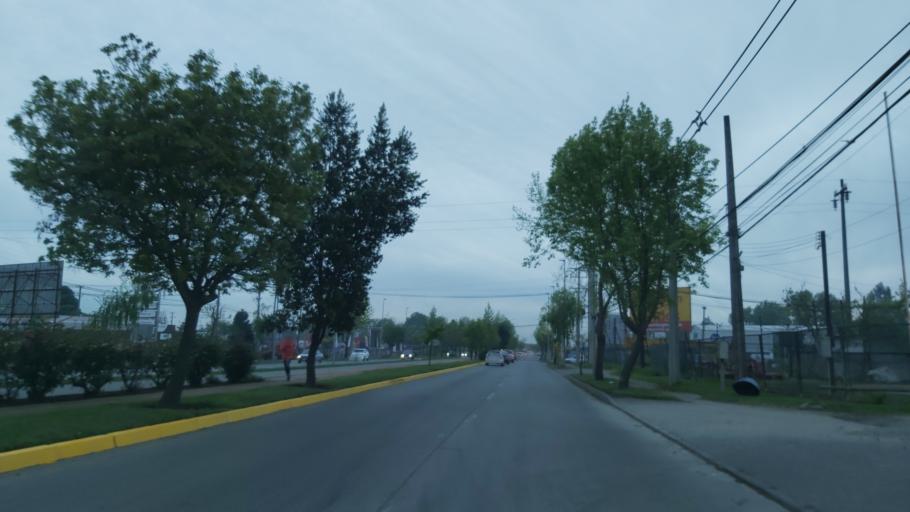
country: CL
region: Maule
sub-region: Provincia de Linares
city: Linares
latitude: -35.8406
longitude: -71.6249
